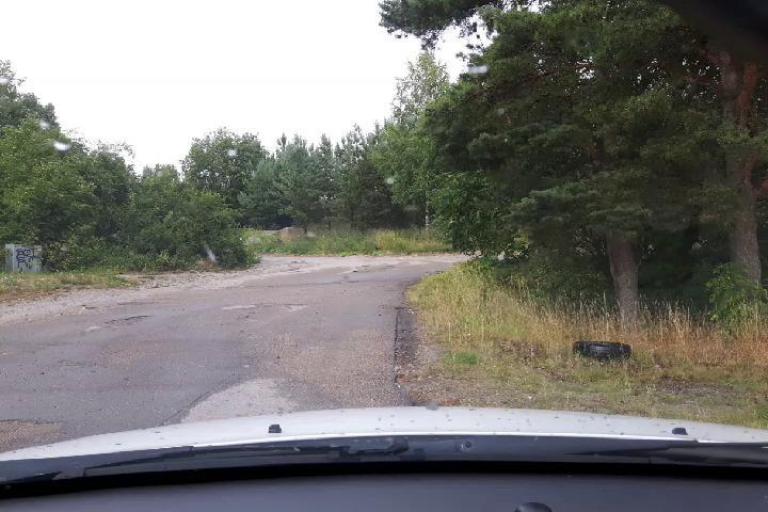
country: SE
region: Uppsala
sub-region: Uppsala Kommun
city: Gamla Uppsala
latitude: 59.9002
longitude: 17.6125
